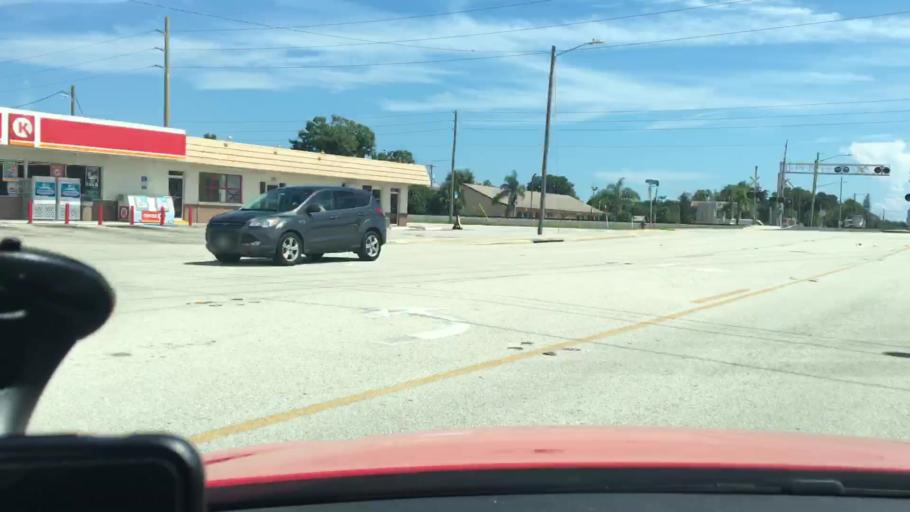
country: US
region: Florida
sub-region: Volusia County
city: Edgewater
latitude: 28.9694
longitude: -80.9032
